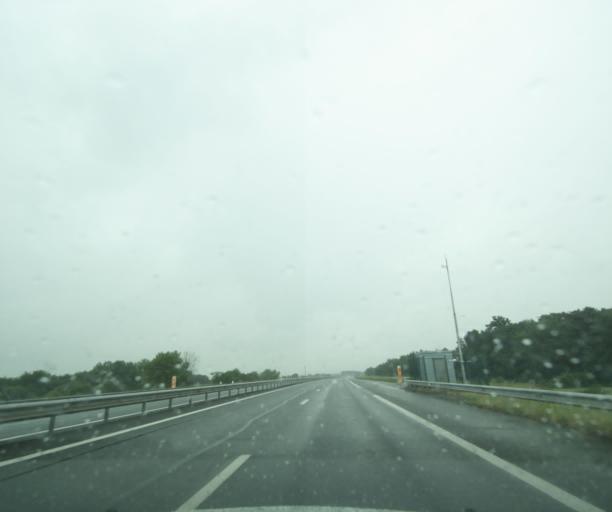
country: FR
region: Auvergne
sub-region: Departement de l'Allier
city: Vallon-en-Sully
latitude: 46.5930
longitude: 2.5155
